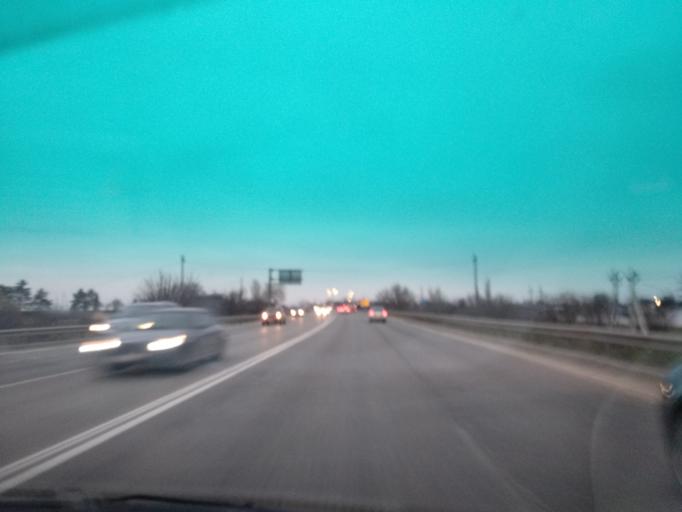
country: RU
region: Krasnodarskiy
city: Pashkovskiy
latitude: 45.0029
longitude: 39.1152
